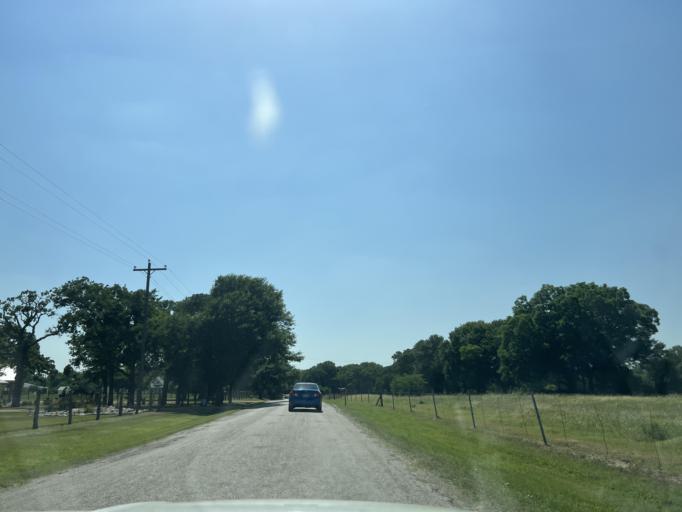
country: US
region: Texas
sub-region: Washington County
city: Brenham
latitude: 30.1566
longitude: -96.5008
